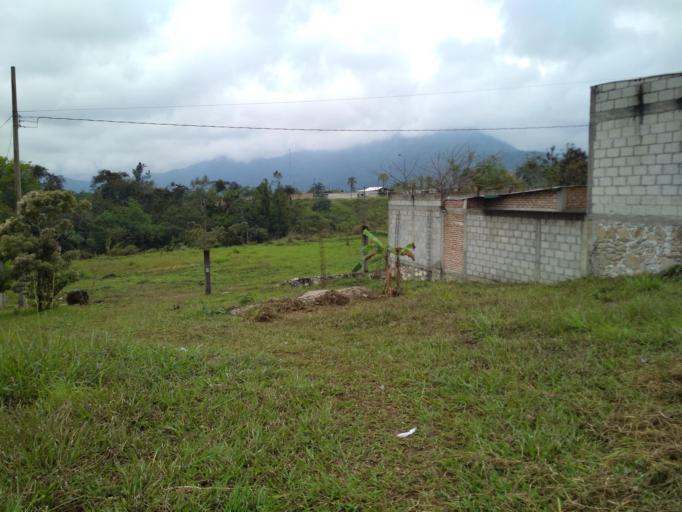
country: MX
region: Veracruz
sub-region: Cordoba
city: San Jose de Tapia
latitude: 18.8490
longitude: -96.9661
